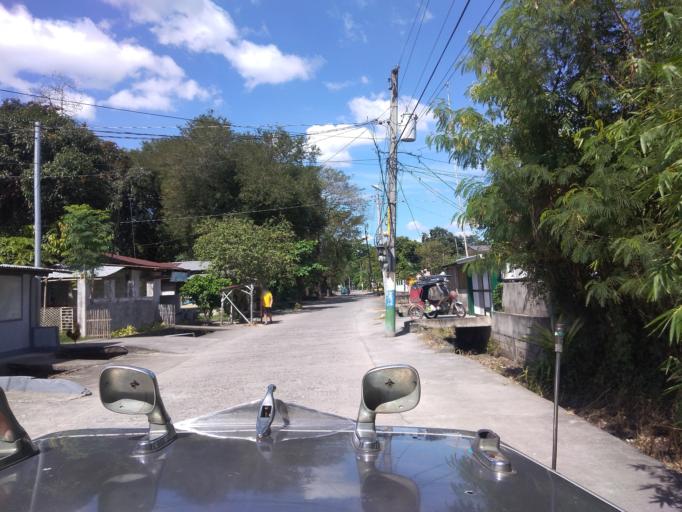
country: PH
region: Central Luzon
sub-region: Province of Pampanga
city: Santa Rita
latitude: 15.0037
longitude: 120.6018
